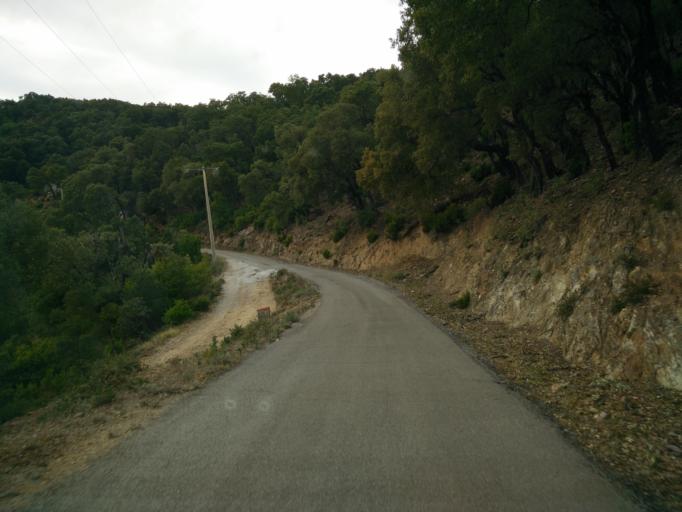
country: FR
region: Provence-Alpes-Cote d'Azur
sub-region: Departement du Var
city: Roquebrune-sur-Argens
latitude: 43.3805
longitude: 6.6183
